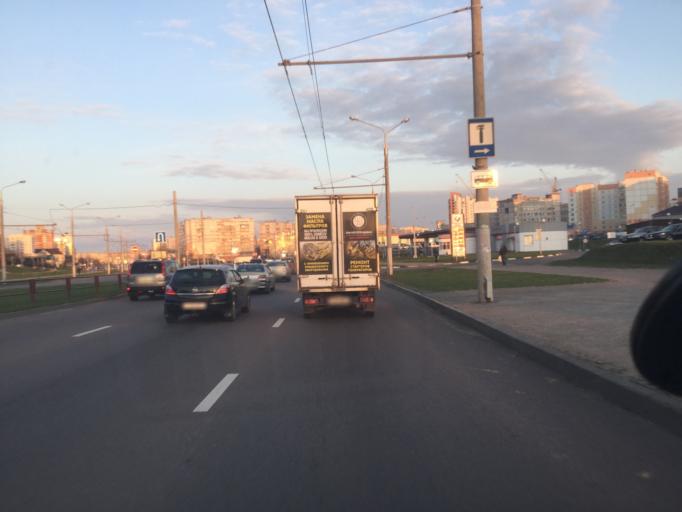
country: BY
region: Vitebsk
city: Vitebsk
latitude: 55.1646
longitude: 30.2029
